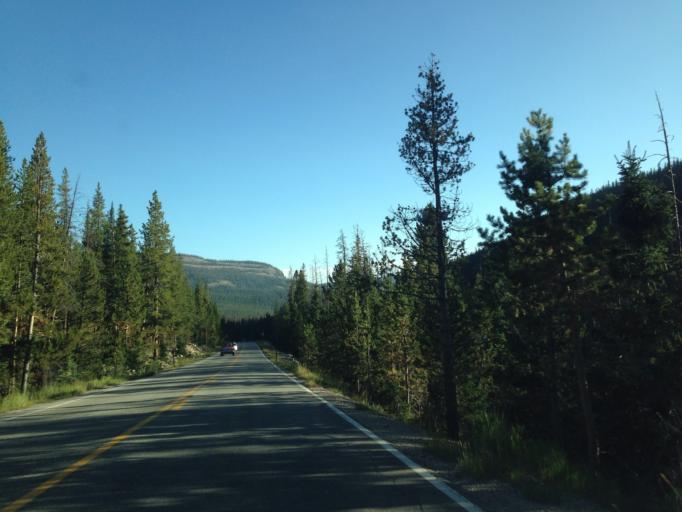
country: US
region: Utah
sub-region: Summit County
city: Kamas
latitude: 40.6541
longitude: -110.9448
